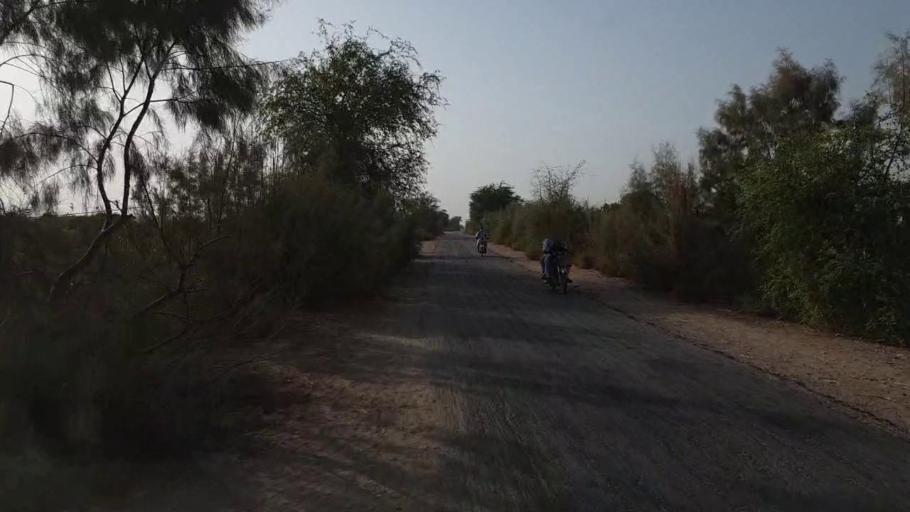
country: PK
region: Sindh
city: Jam Sahib
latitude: 26.4914
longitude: 68.8580
